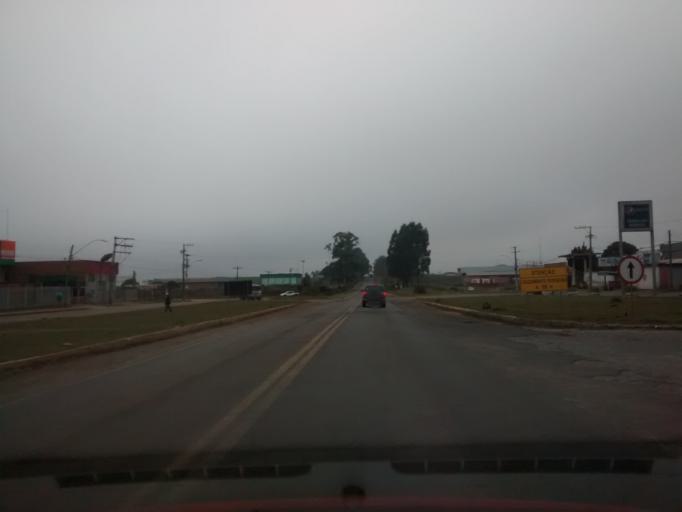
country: BR
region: Rio Grande do Sul
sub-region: Vacaria
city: Vacaria
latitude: -28.4994
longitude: -50.9185
